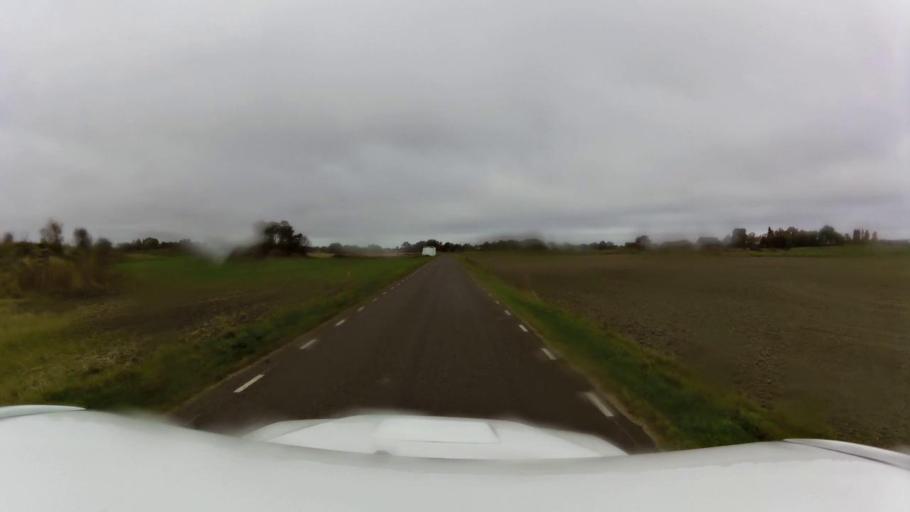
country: SE
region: OEstergoetland
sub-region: Linkopings Kommun
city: Linghem
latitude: 58.4817
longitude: 15.7448
